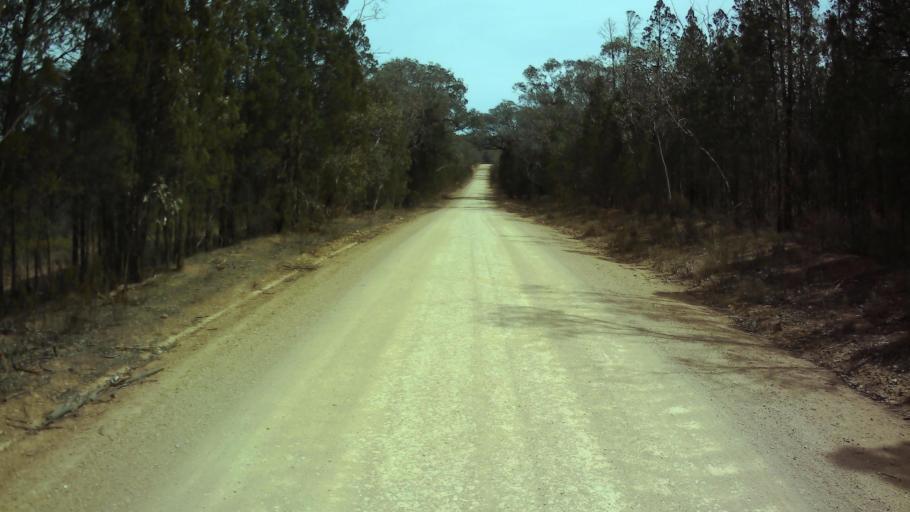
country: AU
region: New South Wales
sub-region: Weddin
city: Grenfell
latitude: -33.9097
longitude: 148.4113
